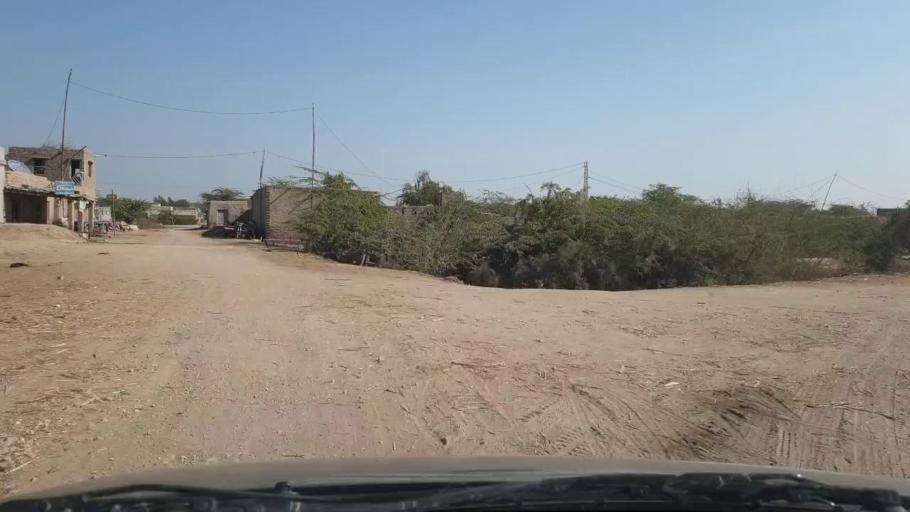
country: PK
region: Sindh
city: Samaro
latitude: 25.2014
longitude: 69.2624
